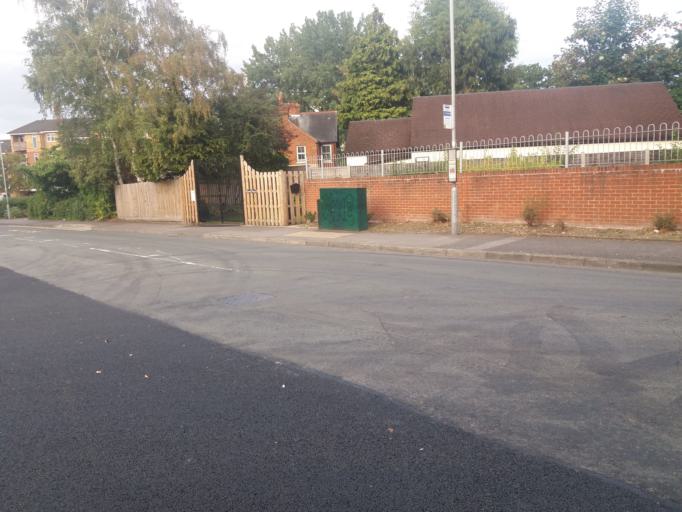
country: GB
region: England
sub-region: Bracknell Forest
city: Bracknell
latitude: 51.4165
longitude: -0.7354
